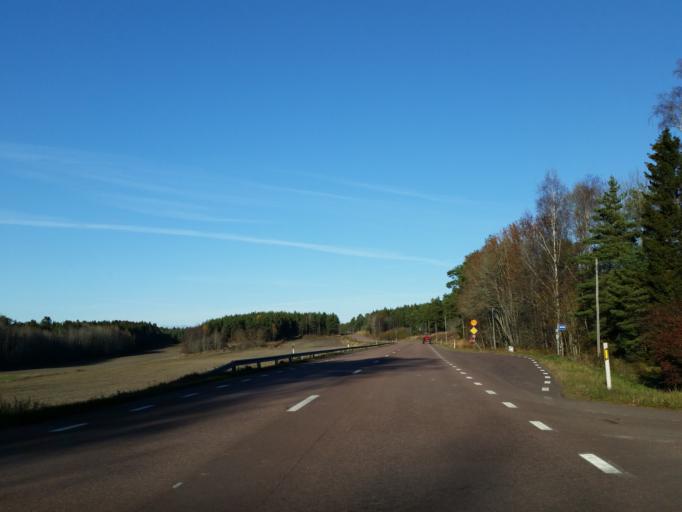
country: AX
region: Alands landsbygd
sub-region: Finstroem
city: Finstroem
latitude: 60.2539
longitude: 19.9630
